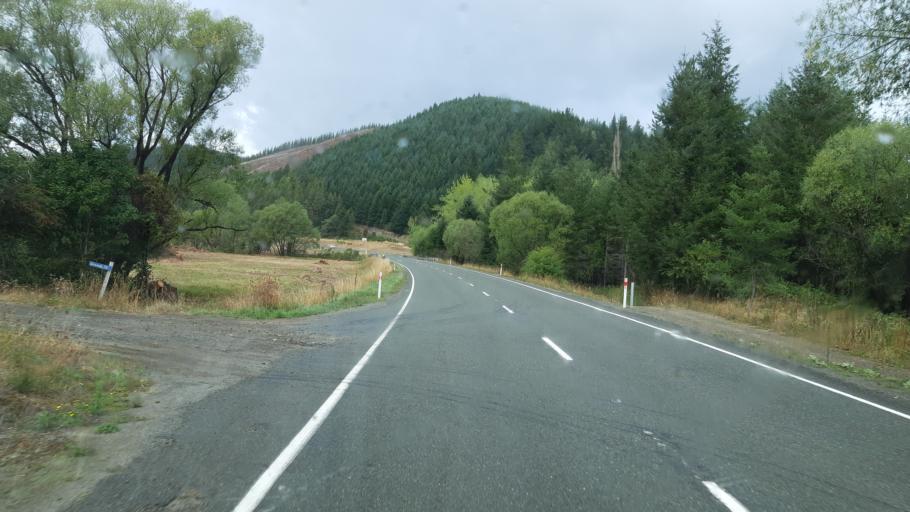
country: NZ
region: Tasman
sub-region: Tasman District
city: Wakefield
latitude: -41.4714
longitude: 172.8426
